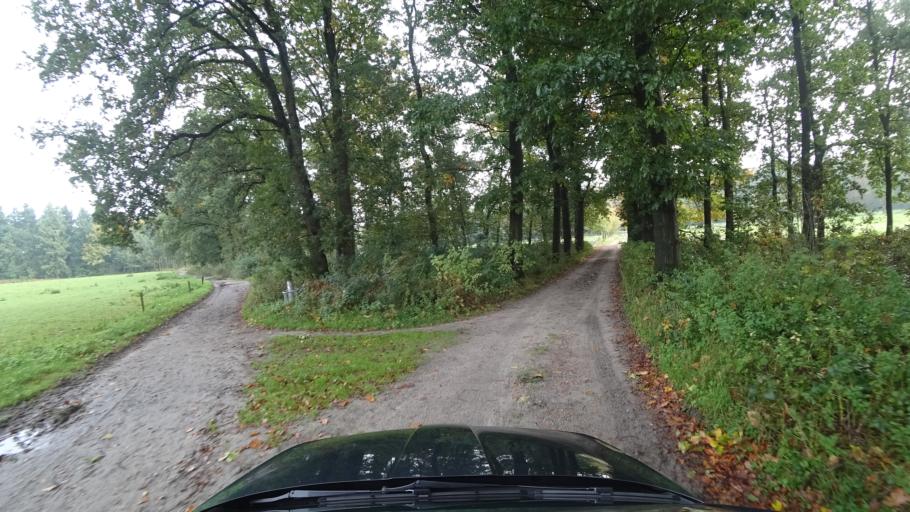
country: NL
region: Gelderland
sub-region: Gemeente Renkum
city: Renkum
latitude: 51.9969
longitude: 5.7312
